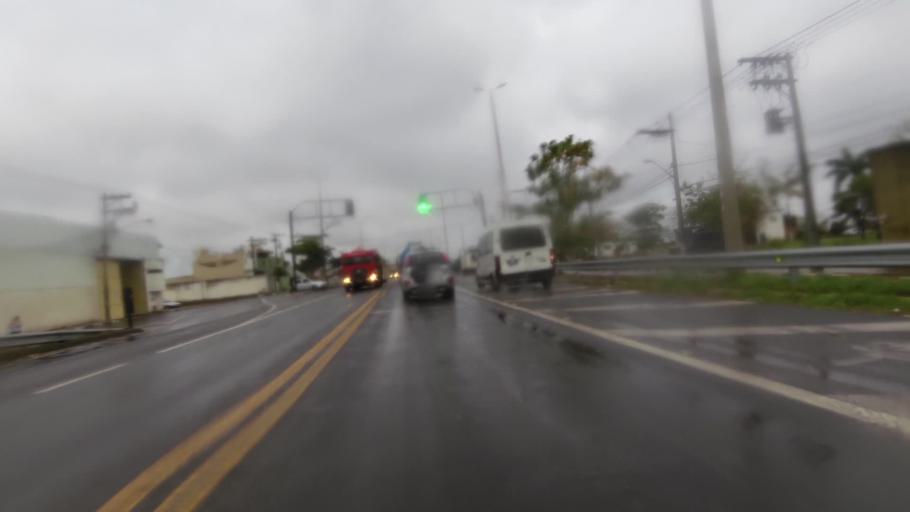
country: BR
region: Rio de Janeiro
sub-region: Campos Dos Goytacazes
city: Campos
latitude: -21.7074
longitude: -41.3093
